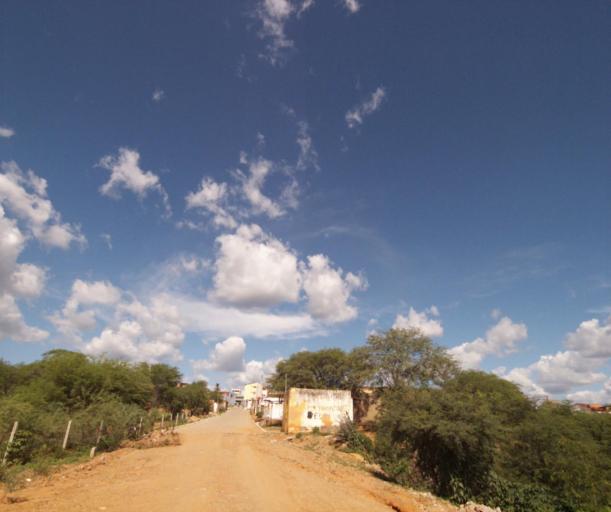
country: BR
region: Bahia
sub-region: Pocoes
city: Pocoes
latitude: -14.2418
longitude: -40.7752
